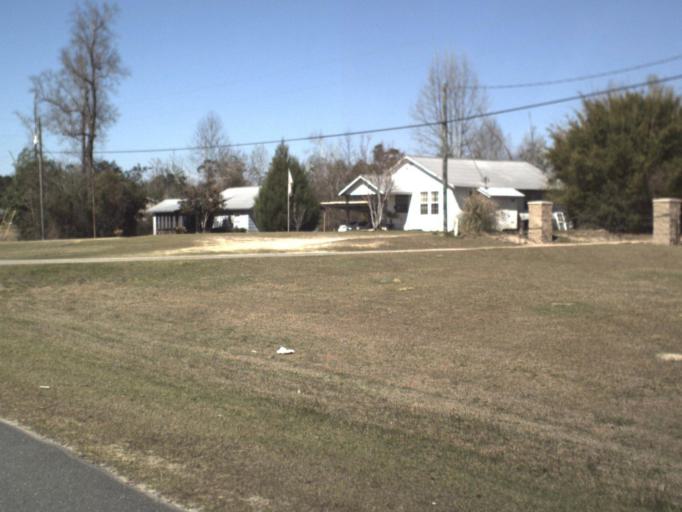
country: US
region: Florida
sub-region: Jackson County
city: Marianna
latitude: 30.7399
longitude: -85.1417
